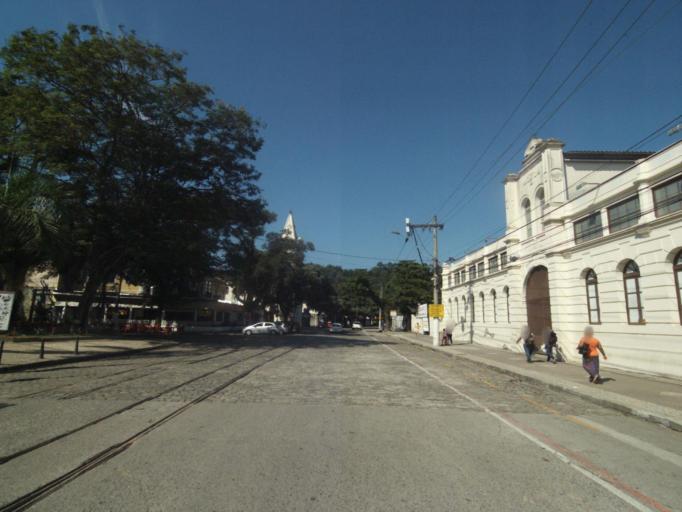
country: BR
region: Rio de Janeiro
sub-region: Niteroi
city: Niteroi
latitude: -22.8993
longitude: -43.1308
